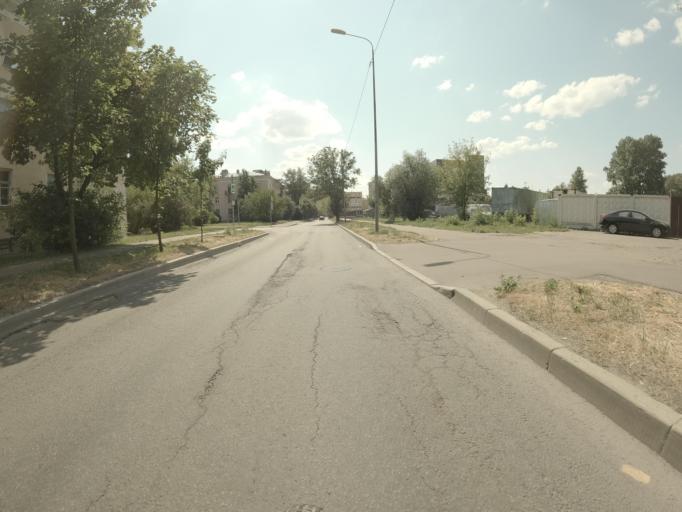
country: RU
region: St.-Petersburg
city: Avtovo
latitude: 59.8910
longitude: 30.2613
